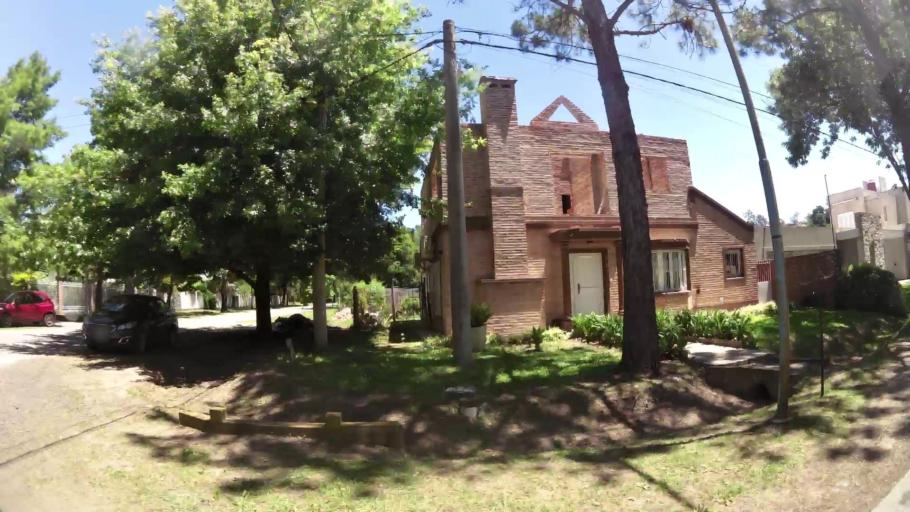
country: AR
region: Santa Fe
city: Rafaela
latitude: -31.2581
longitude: -61.4544
